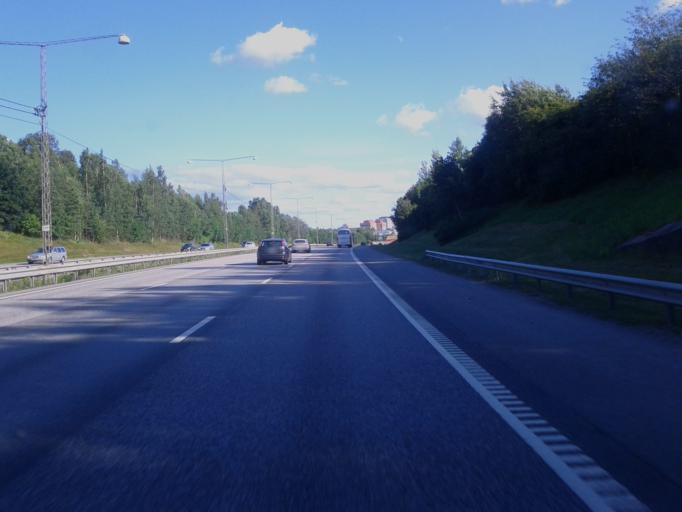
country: SE
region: Stockholm
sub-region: Sollentuna Kommun
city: Sollentuna
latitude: 59.4544
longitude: 17.9154
